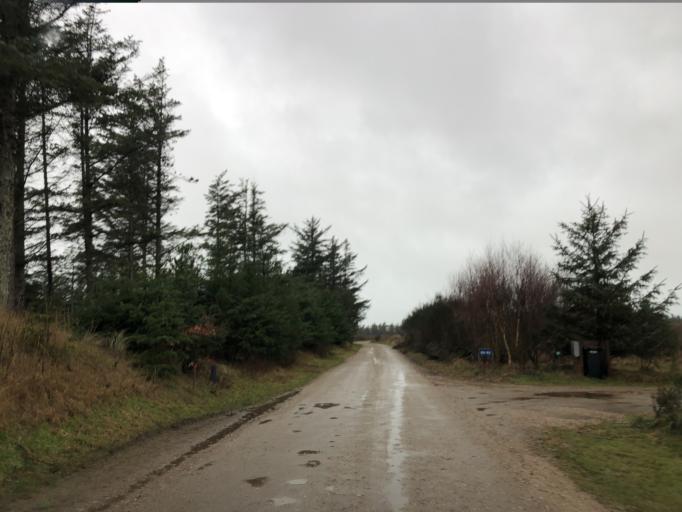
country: DK
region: Central Jutland
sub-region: Holstebro Kommune
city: Ulfborg
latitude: 56.2789
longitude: 8.1462
